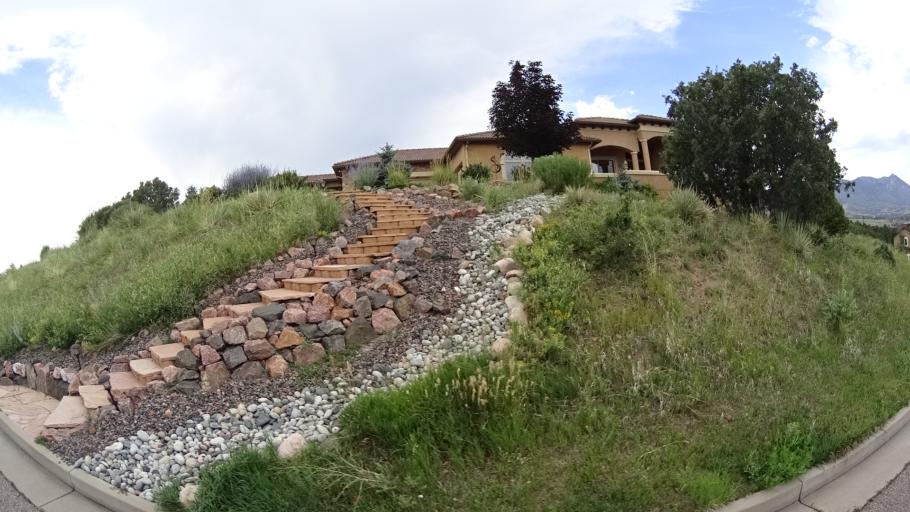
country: US
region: Colorado
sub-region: El Paso County
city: Colorado Springs
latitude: 38.9098
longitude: -104.8328
